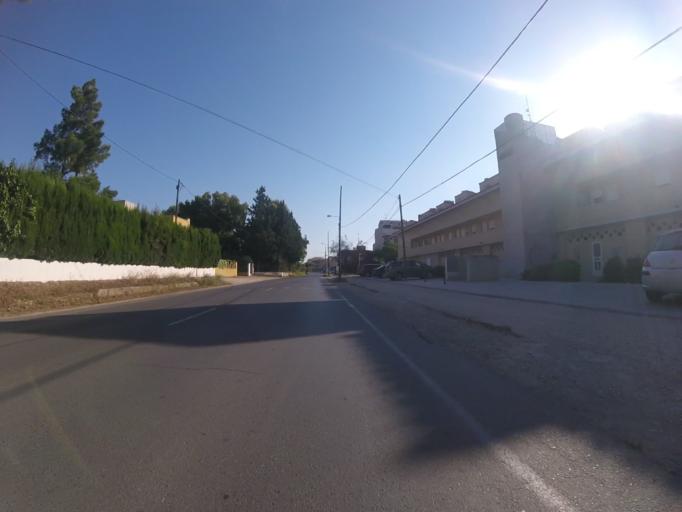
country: ES
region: Valencia
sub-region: Provincia de Castello
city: Benicarlo
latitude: 40.4110
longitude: 0.4209
